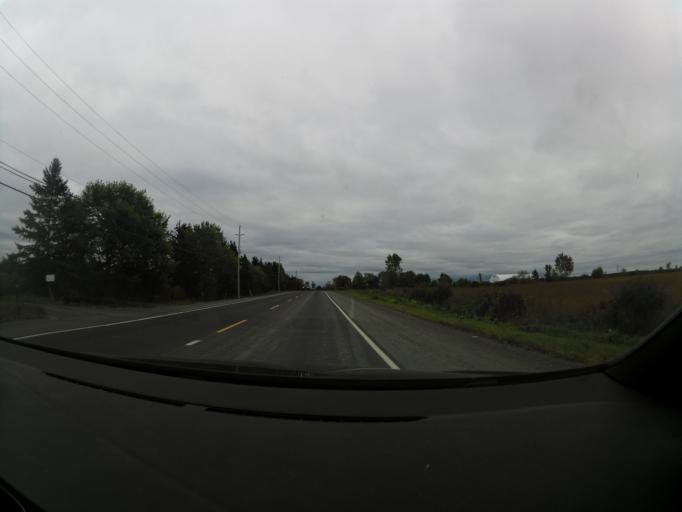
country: CA
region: Ontario
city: Bells Corners
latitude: 45.4103
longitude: -76.0062
